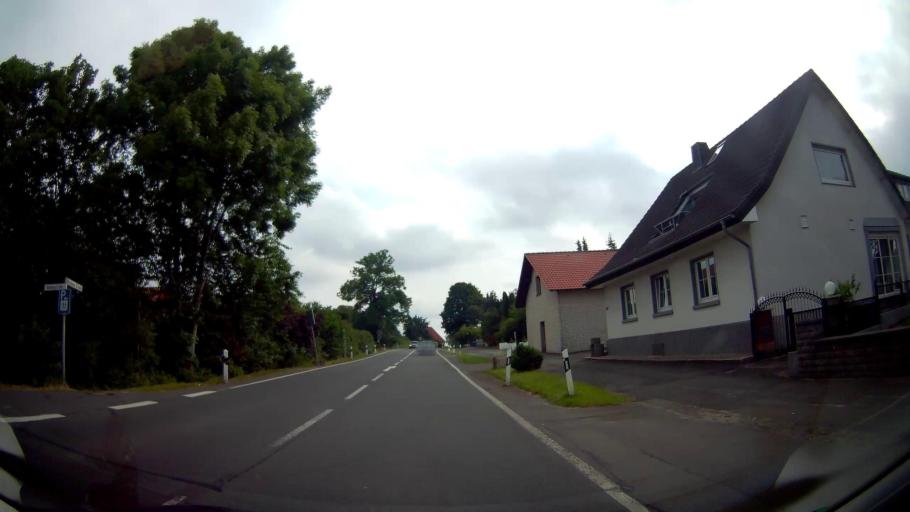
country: DE
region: North Rhine-Westphalia
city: Loehne
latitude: 52.1469
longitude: 8.7048
